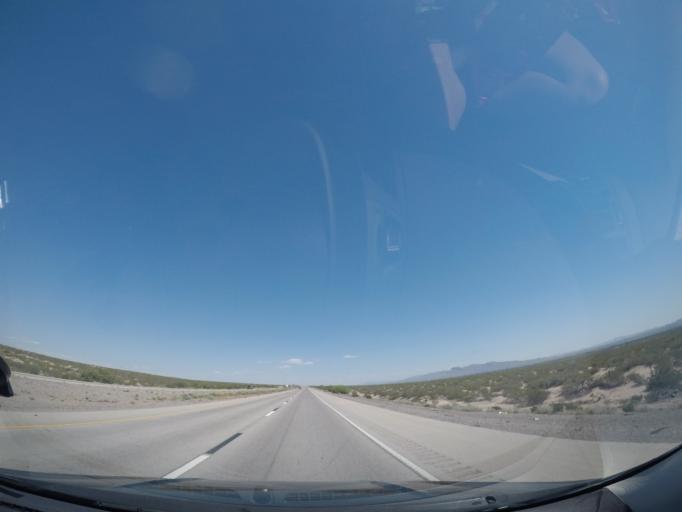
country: US
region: Texas
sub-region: El Paso County
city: Tornillo
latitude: 31.4596
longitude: -106.0472
